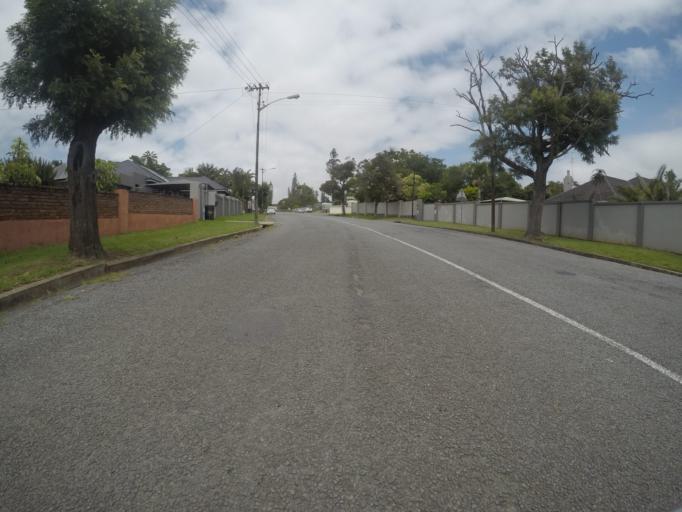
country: ZA
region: Eastern Cape
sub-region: Buffalo City Metropolitan Municipality
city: East London
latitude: -32.9902
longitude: 27.9249
